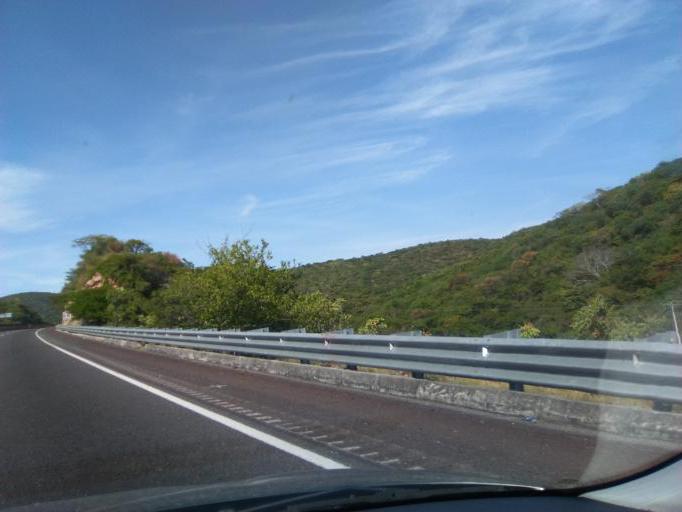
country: MX
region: Guerrero
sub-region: Huitzuco de los Figueroa
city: Ciudad de Huitzuco
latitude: 18.1575
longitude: -99.2129
